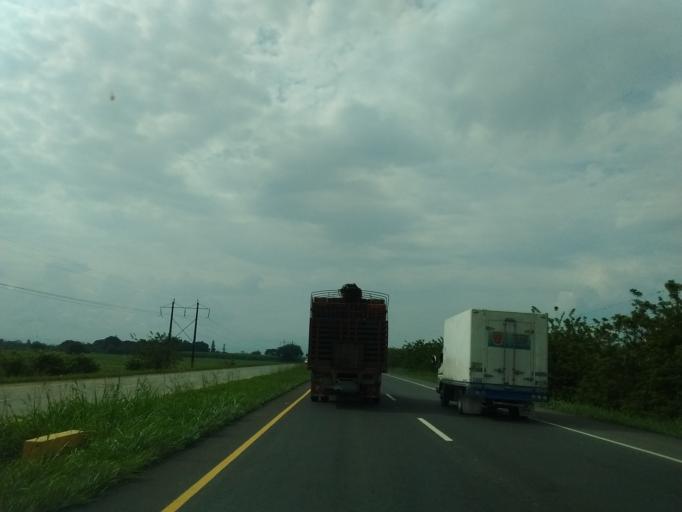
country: CO
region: Cauca
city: Caloto
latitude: 3.1115
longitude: -76.4672
